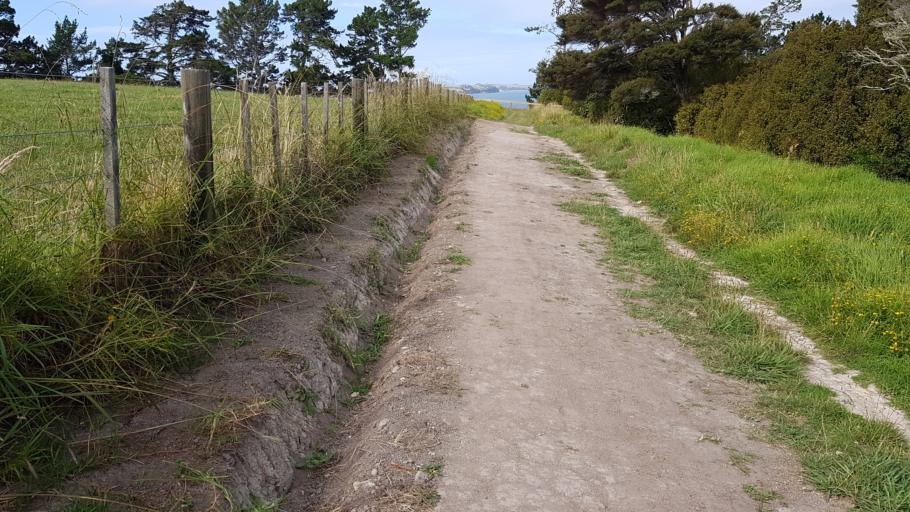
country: NZ
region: Auckland
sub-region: Auckland
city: Rothesay Bay
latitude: -36.6652
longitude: 174.7476
